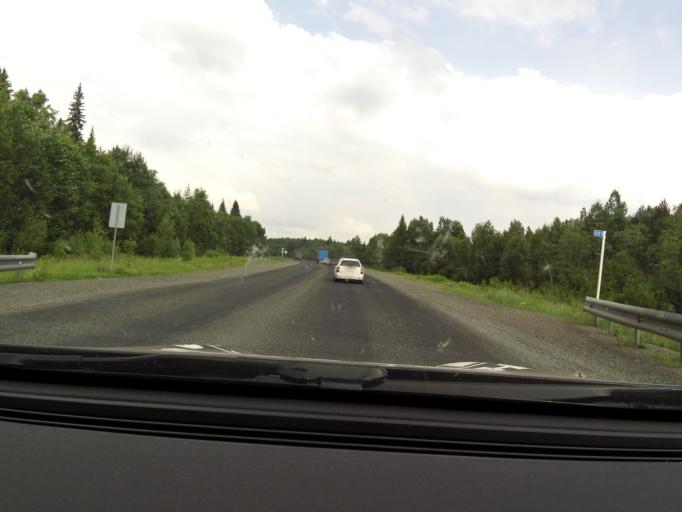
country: RU
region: Sverdlovsk
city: Ufimskiy
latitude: 56.7631
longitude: 58.1570
